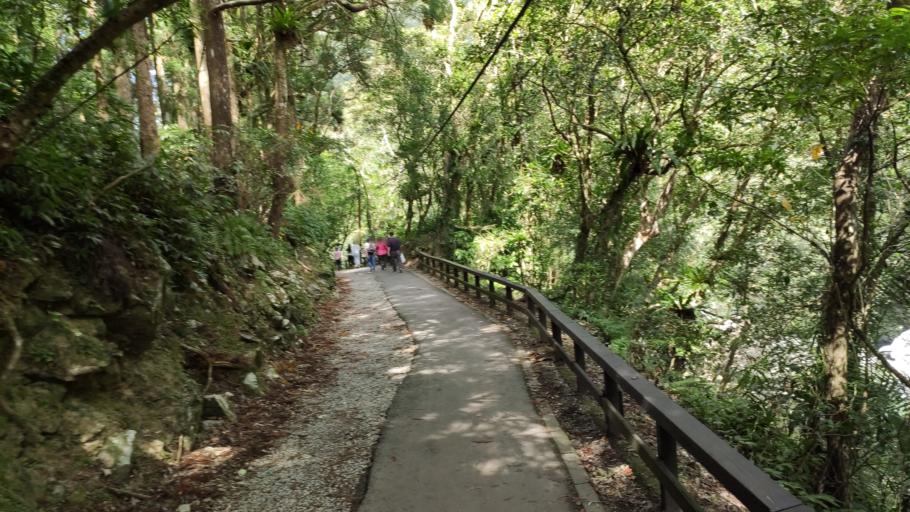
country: TW
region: Taiwan
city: Daxi
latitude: 24.8246
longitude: 121.4493
